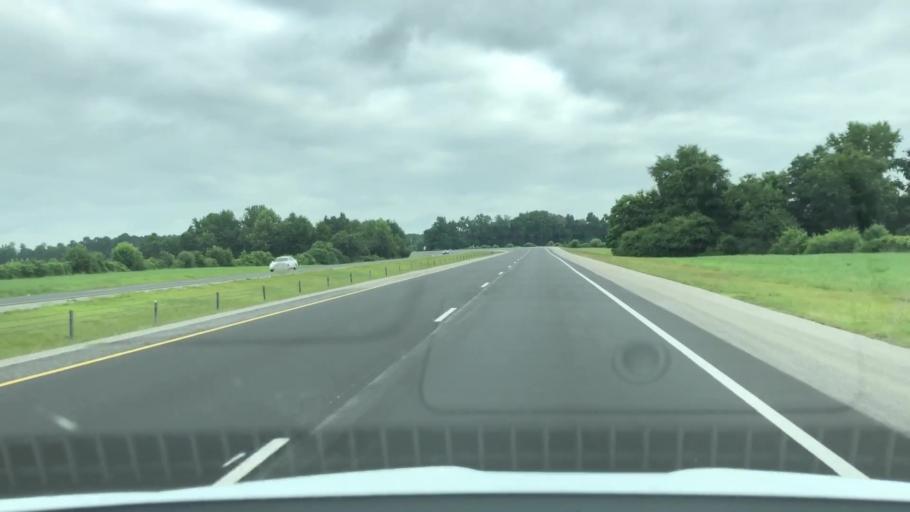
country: US
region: North Carolina
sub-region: Wayne County
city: Fremont
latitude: 35.5918
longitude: -77.9843
